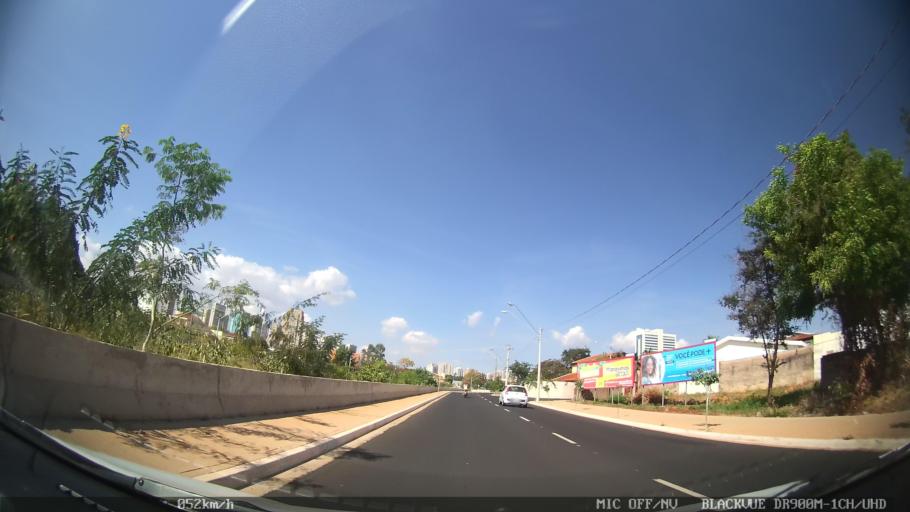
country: BR
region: Sao Paulo
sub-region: Ribeirao Preto
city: Ribeirao Preto
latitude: -21.2052
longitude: -47.8174
